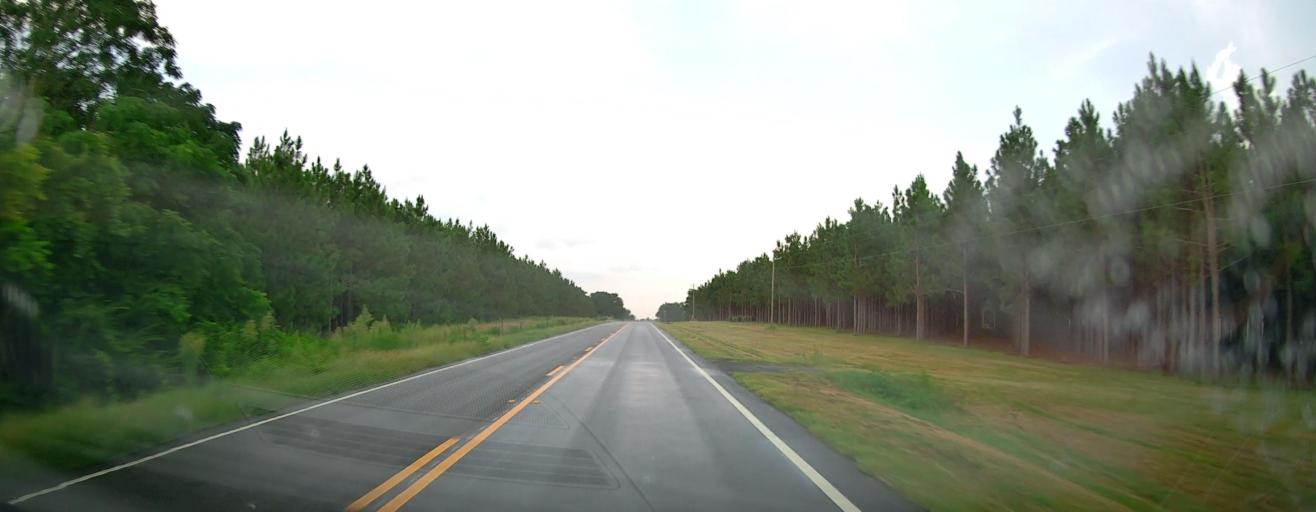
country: US
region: Georgia
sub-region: Dodge County
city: Chester
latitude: 32.5502
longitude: -83.1307
